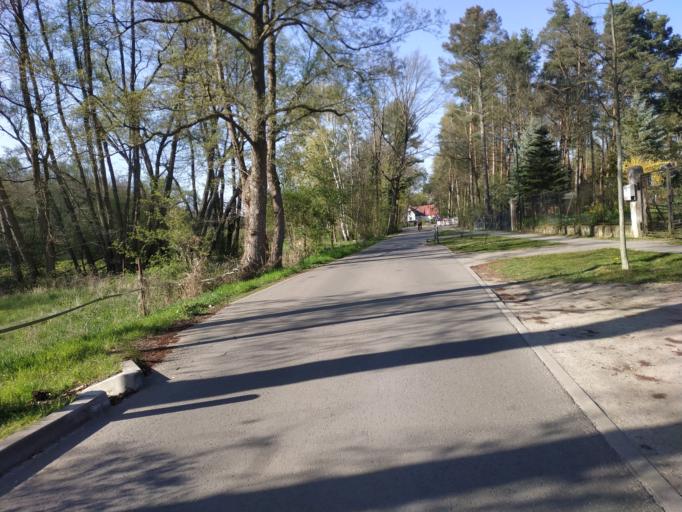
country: DE
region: Brandenburg
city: Petershagen
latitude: 52.5494
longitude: 13.8245
